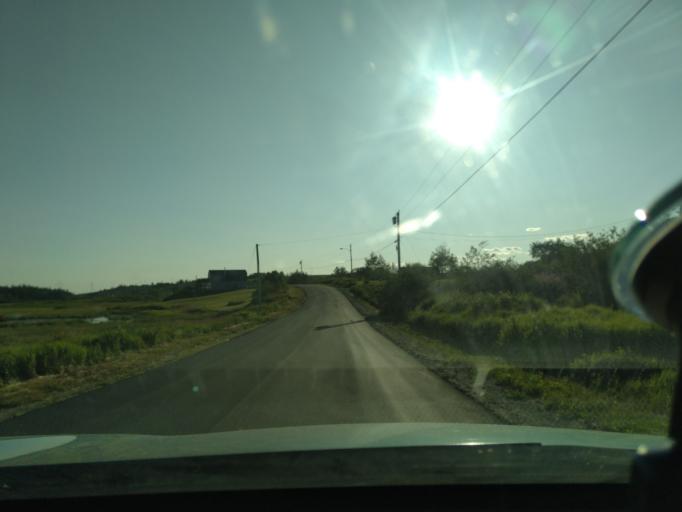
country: US
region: Maine
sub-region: Washington County
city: Machiasport
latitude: 44.6869
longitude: -67.1711
